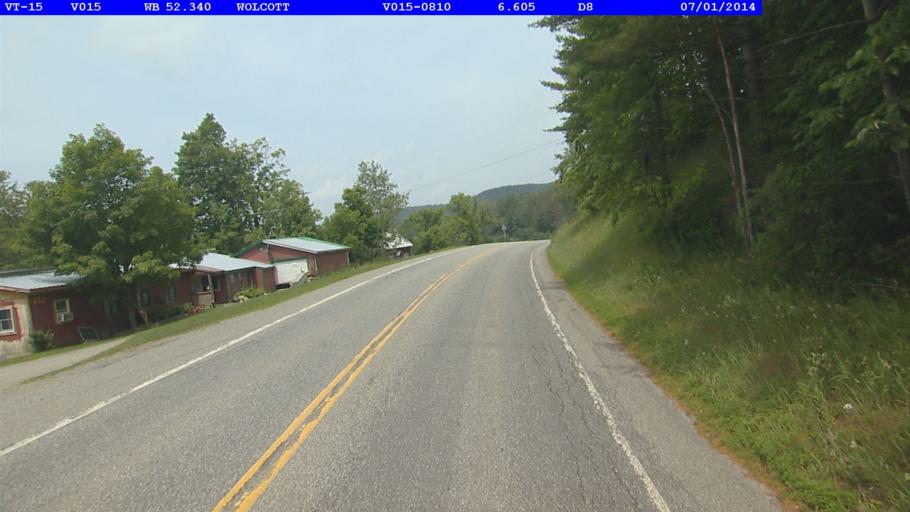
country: US
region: Vermont
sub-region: Caledonia County
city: Hardwick
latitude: 44.5298
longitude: -72.4239
